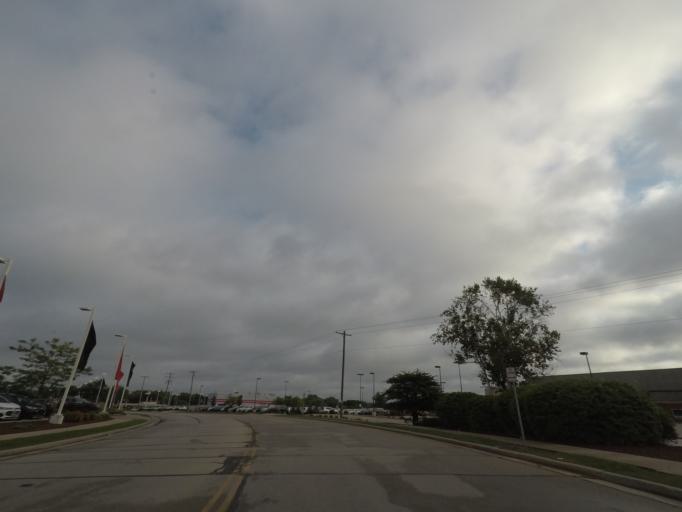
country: US
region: Wisconsin
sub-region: Waukesha County
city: Waukesha
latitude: 43.0229
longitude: -88.2067
